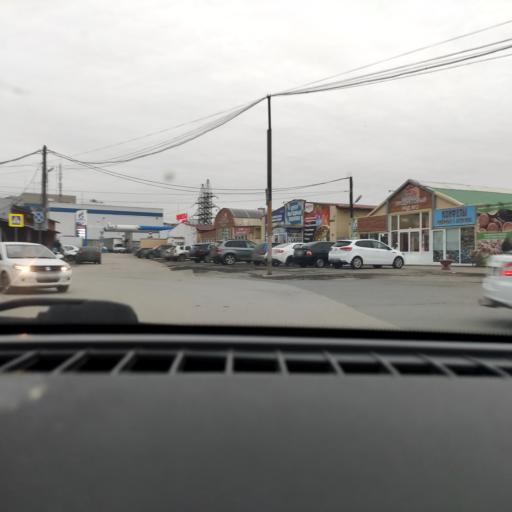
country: RU
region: Perm
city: Perm
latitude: 58.0007
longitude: 56.2293
